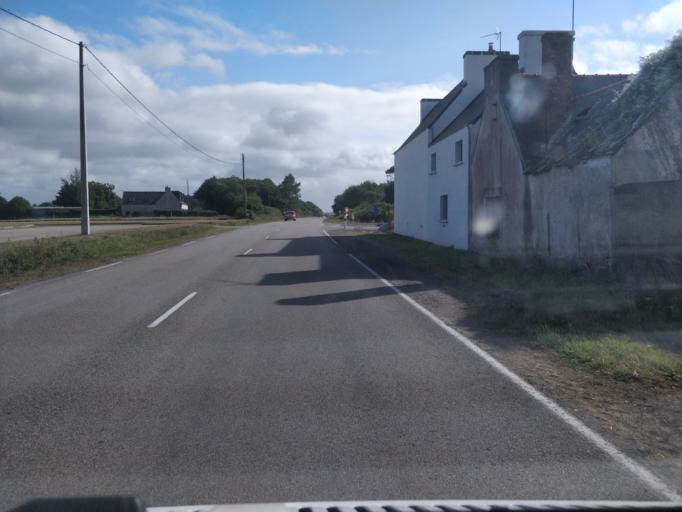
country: FR
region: Brittany
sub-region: Departement du Finistere
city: Plozevet
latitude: 47.9948
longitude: -4.3947
